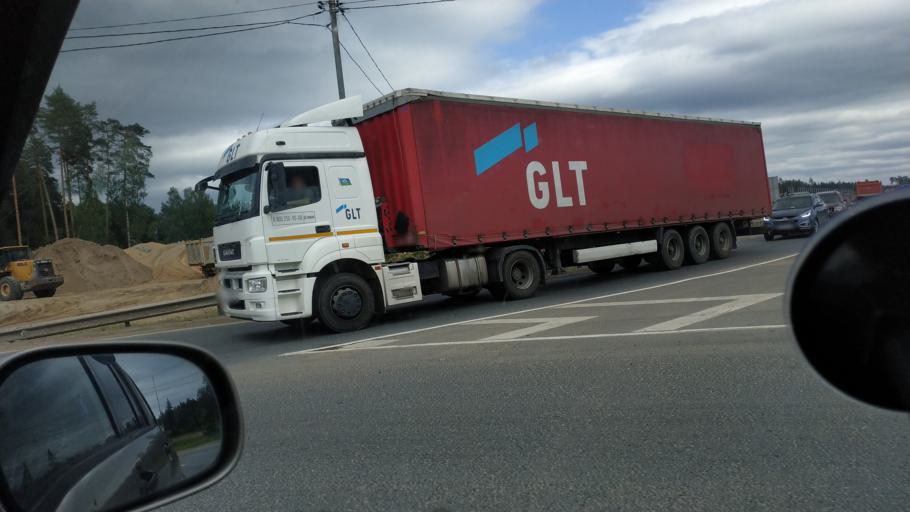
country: RU
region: Moskovskaya
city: Krasnoarmeysk
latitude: 56.0386
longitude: 38.1983
